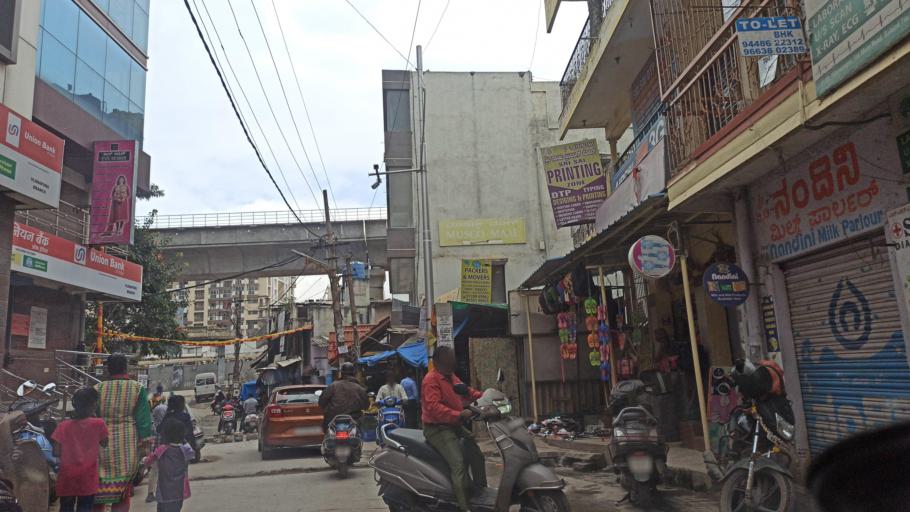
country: IN
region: Karnataka
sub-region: Bangalore Urban
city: Bangalore
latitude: 12.9970
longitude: 77.6719
